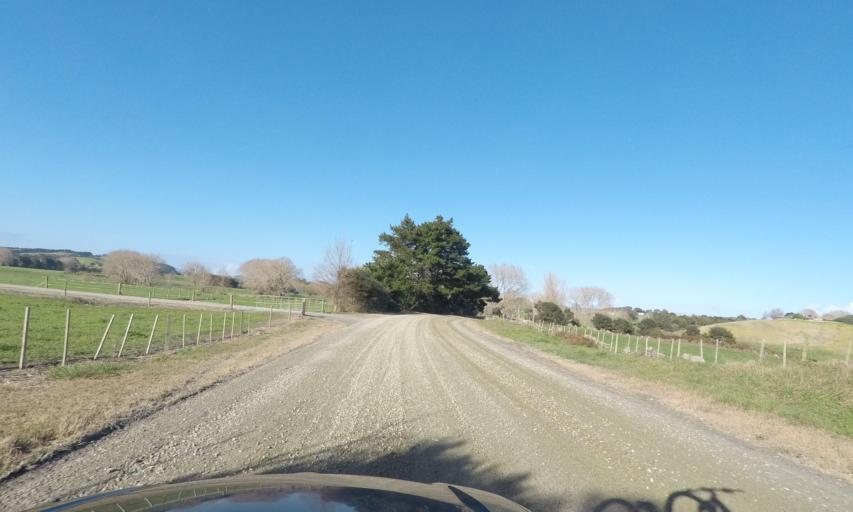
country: NZ
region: Auckland
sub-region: Auckland
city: Wellsford
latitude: -36.1497
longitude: 174.6066
